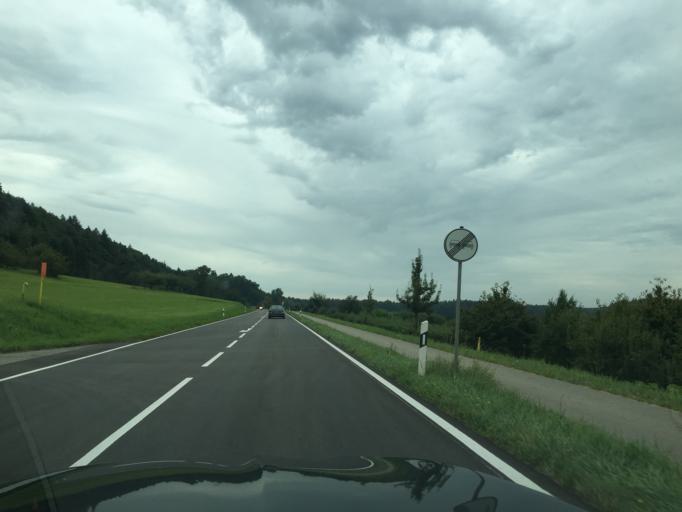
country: DE
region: Baden-Wuerttemberg
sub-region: Freiburg Region
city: Steisslingen
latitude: 47.7896
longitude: 8.9795
